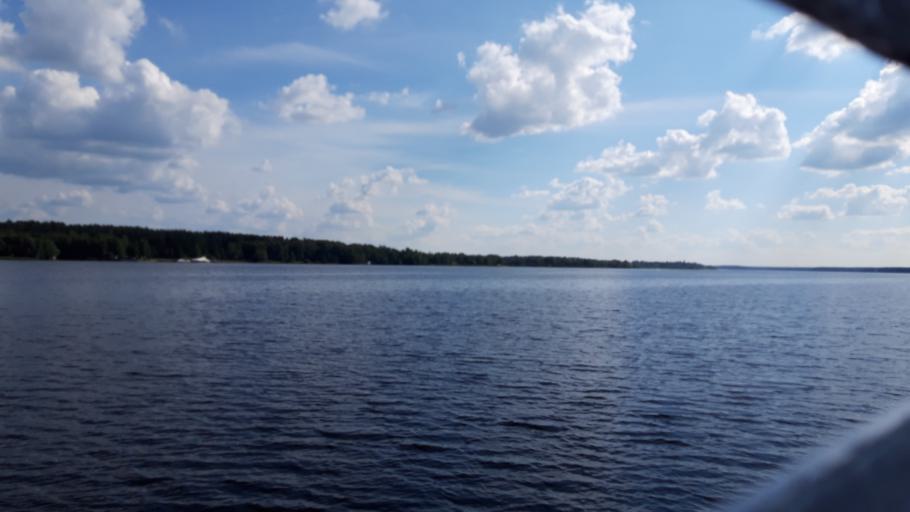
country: RU
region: Tverskaya
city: Konakovo
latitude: 56.6597
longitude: 36.6430
